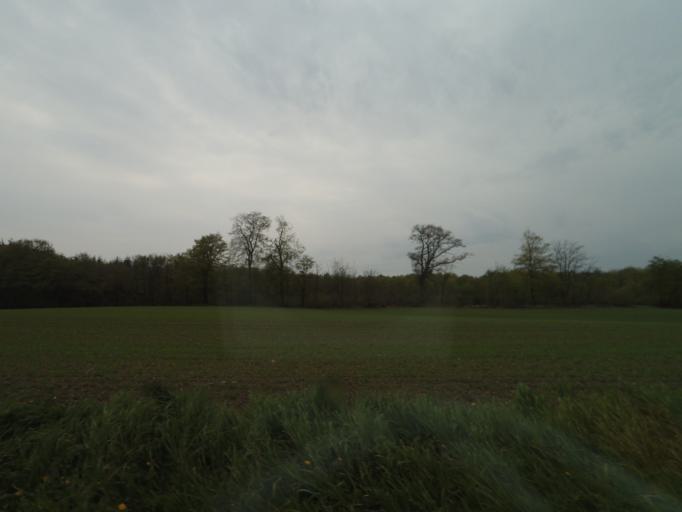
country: DK
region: South Denmark
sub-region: Svendborg Kommune
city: Svendborg
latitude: 55.1663
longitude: 10.6408
